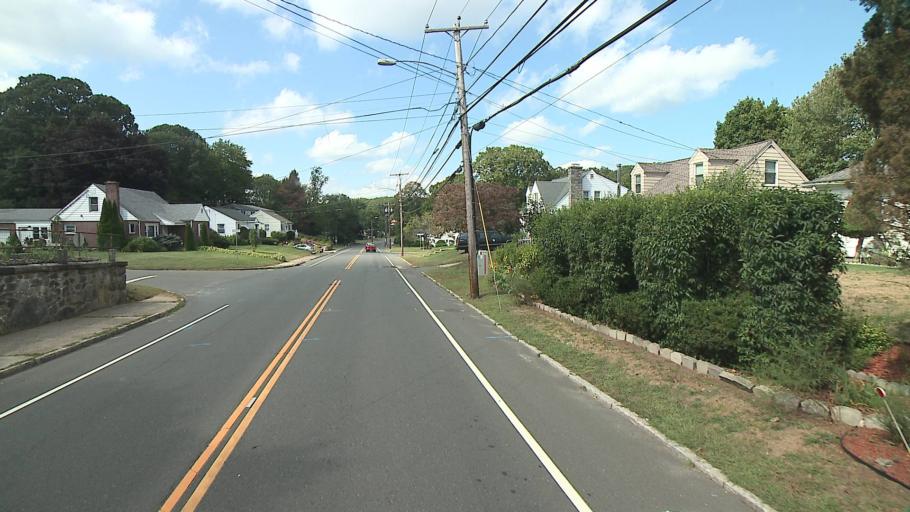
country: US
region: Connecticut
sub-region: New Haven County
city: Ansonia
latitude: 41.3593
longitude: -73.0817
